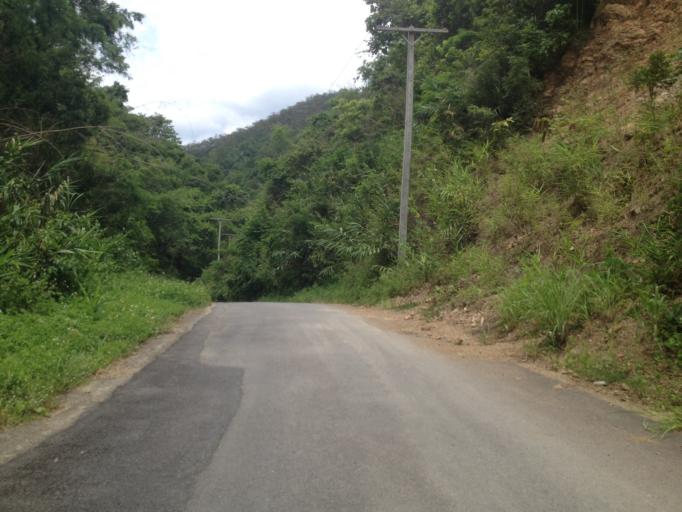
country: TH
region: Chiang Mai
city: Hang Dong
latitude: 18.7177
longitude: 98.8415
